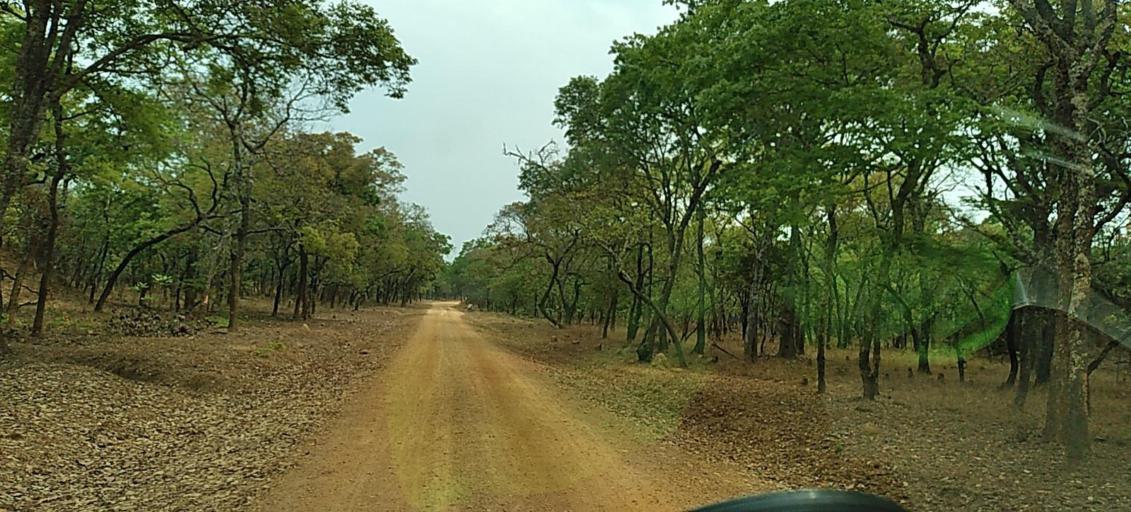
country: ZM
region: North-Western
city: Solwezi
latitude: -12.9259
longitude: 26.5612
